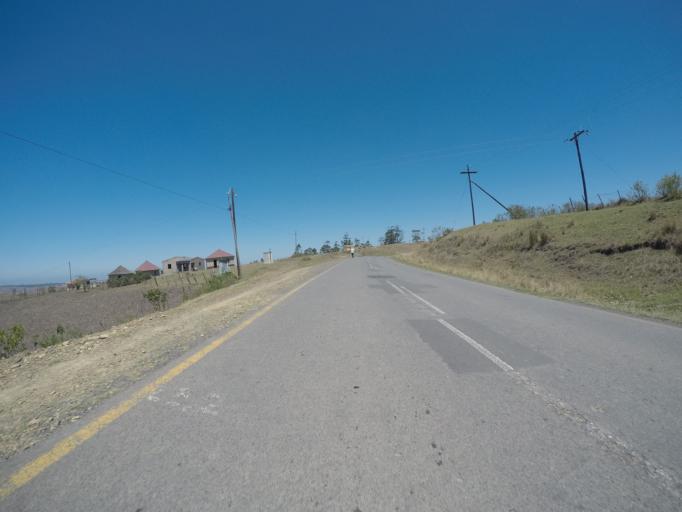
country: ZA
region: Eastern Cape
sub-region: OR Tambo District Municipality
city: Libode
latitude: -31.9151
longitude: 28.9823
